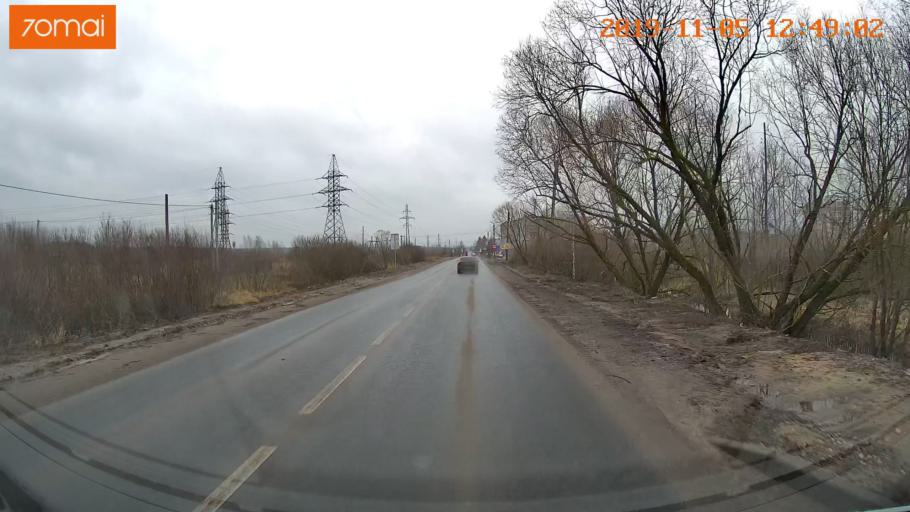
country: RU
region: Ivanovo
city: Kokhma
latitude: 56.9574
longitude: 41.1018
